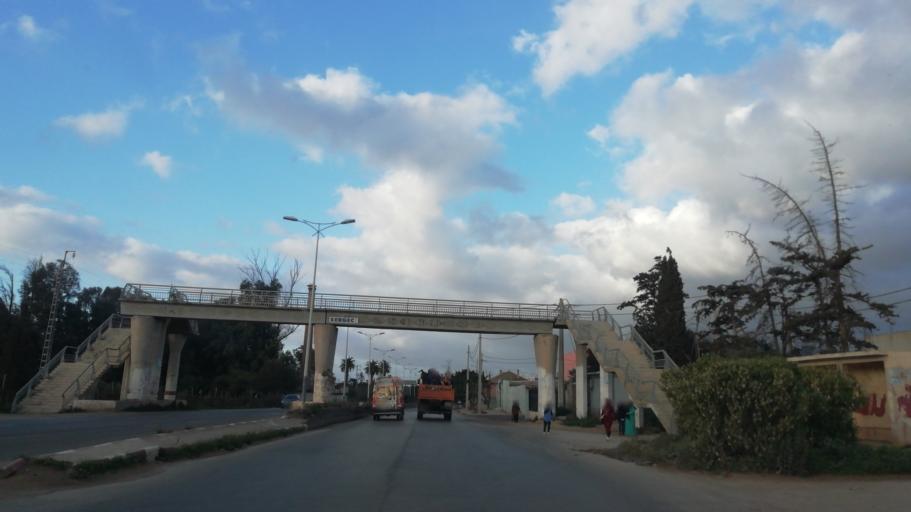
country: DZ
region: Oran
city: Bou Tlelis
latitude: 35.5770
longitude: -0.8455
